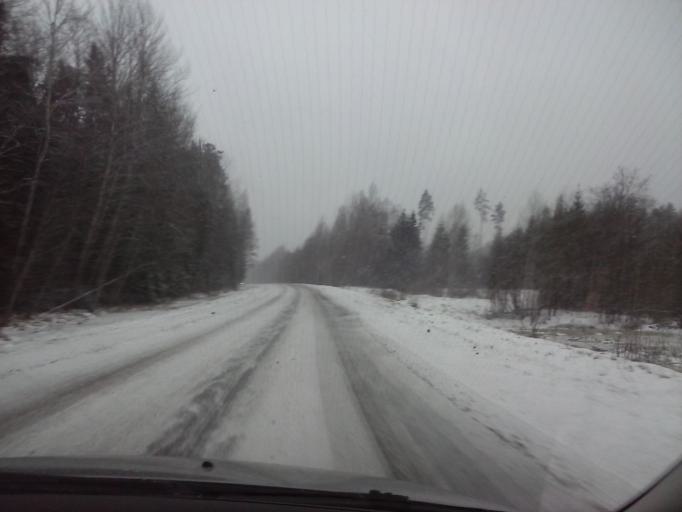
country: LV
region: Valkas Rajons
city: Valka
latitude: 57.7257
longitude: 25.9365
